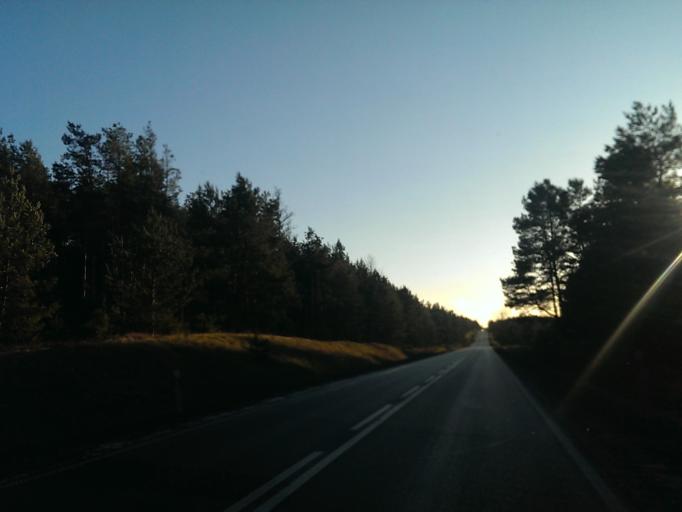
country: PL
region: Kujawsko-Pomorskie
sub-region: Powiat nakielski
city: Naklo nad Notecia
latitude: 53.0962
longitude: 17.5927
